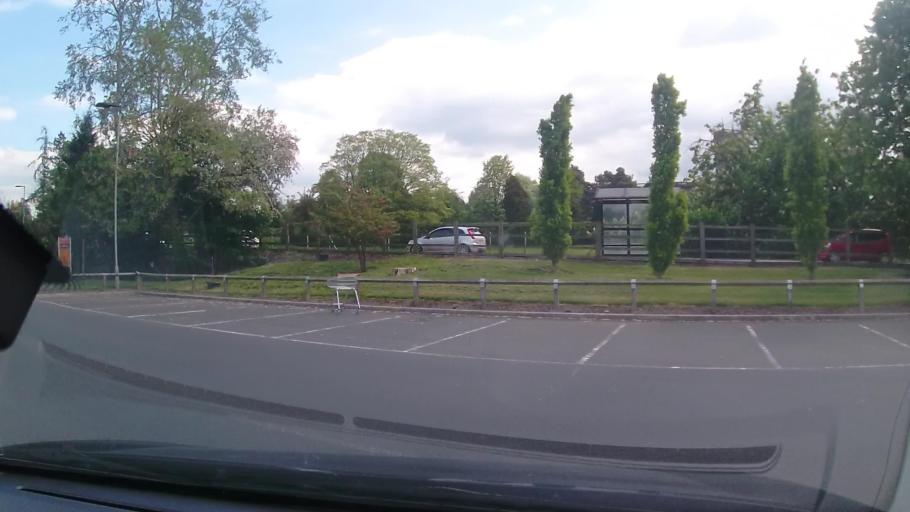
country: GB
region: England
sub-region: Shropshire
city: Whitchurch
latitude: 52.9714
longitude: -2.6862
